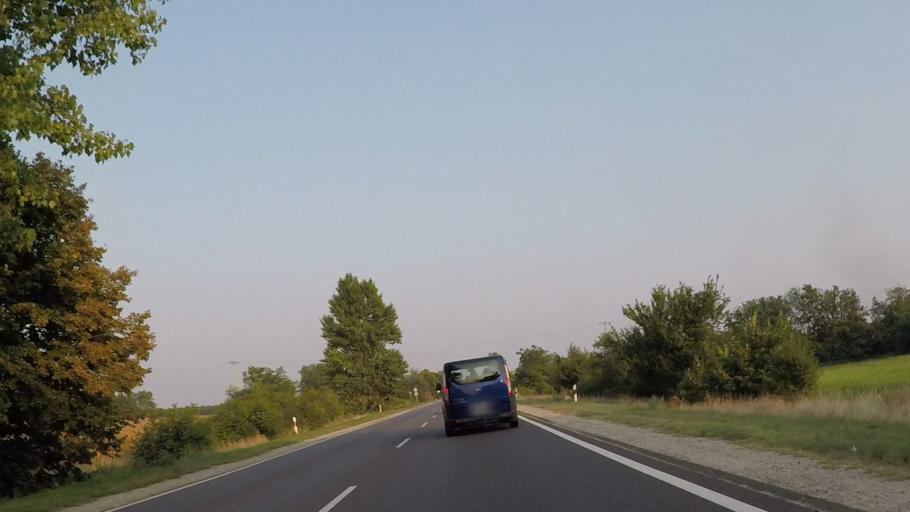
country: HU
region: Pest
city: Albertirsa
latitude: 47.2581
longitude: 19.6268
